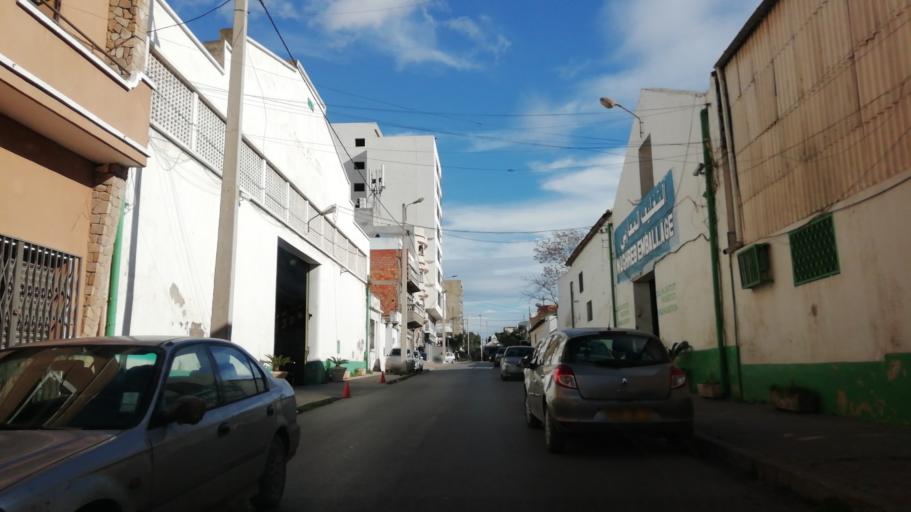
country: DZ
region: Oran
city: Oran
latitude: 35.7002
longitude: -0.6195
